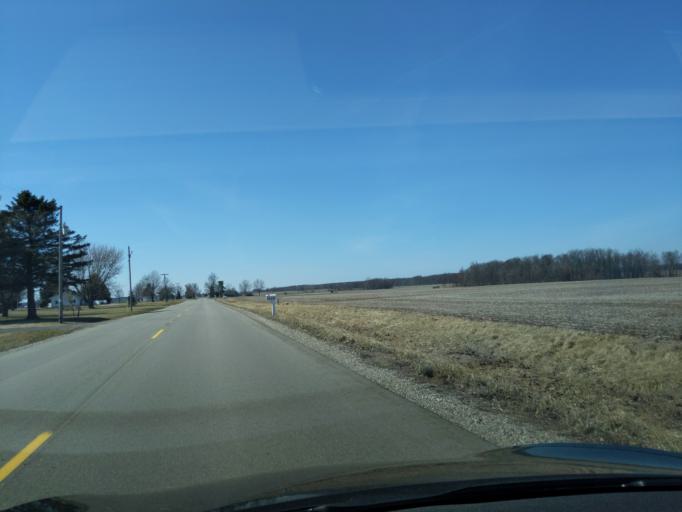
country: US
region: Michigan
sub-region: Eaton County
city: Grand Ledge
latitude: 42.7266
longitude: -84.8474
